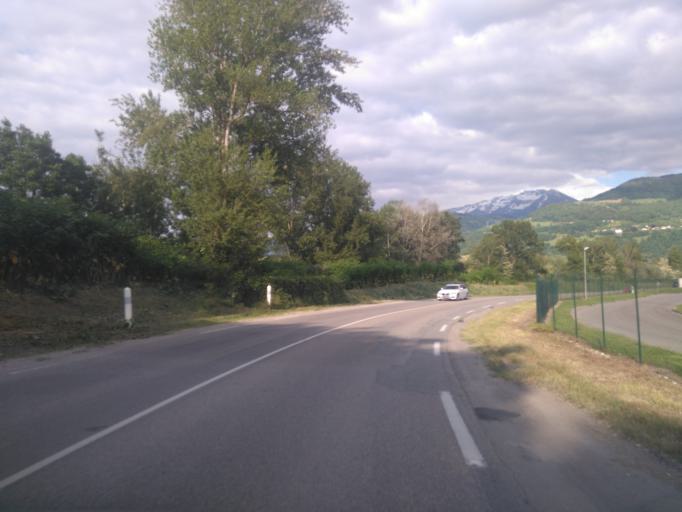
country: FR
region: Rhone-Alpes
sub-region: Departement de l'Isere
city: Saint-Nazaire-les-Eymes
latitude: 45.2367
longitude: 5.8592
